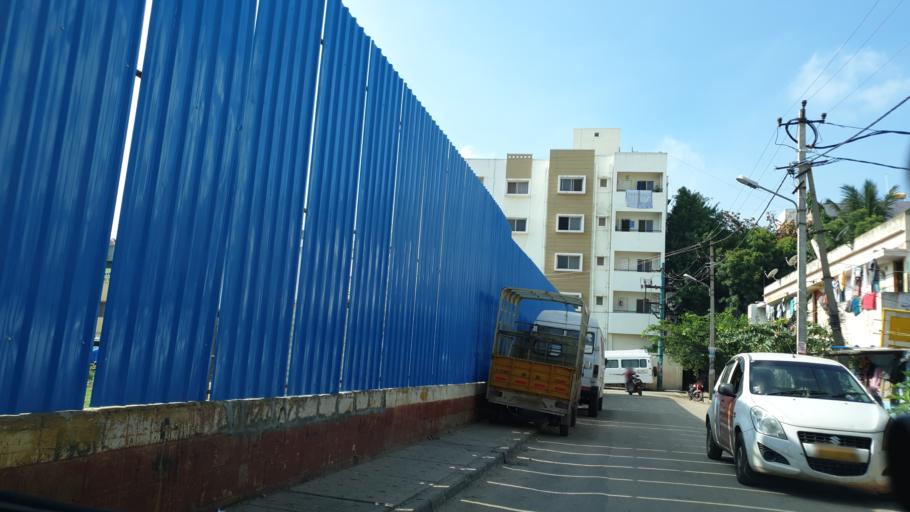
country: IN
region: Karnataka
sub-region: Bangalore Urban
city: Bangalore
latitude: 12.9702
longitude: 77.6703
